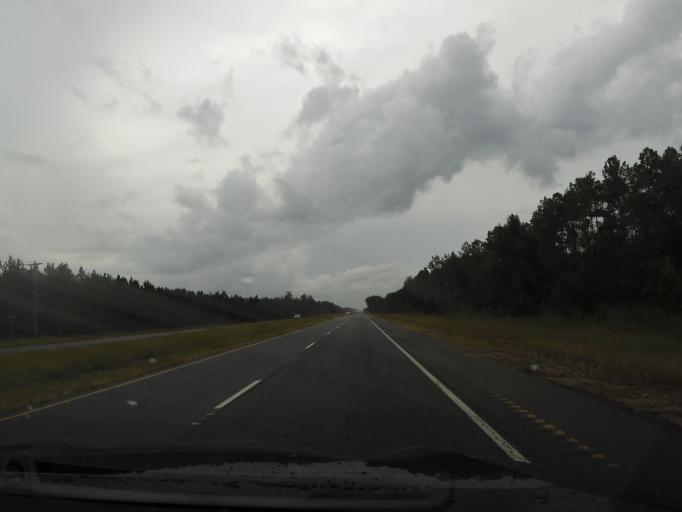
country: US
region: Georgia
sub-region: McIntosh County
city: Darien
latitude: 31.4362
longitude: -81.6813
